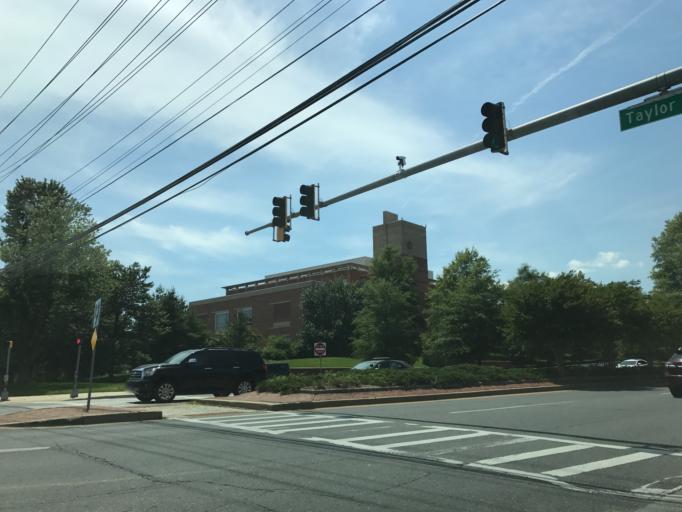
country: US
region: Maryland
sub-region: Anne Arundel County
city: Annapolis
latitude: 38.9873
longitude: -76.5028
